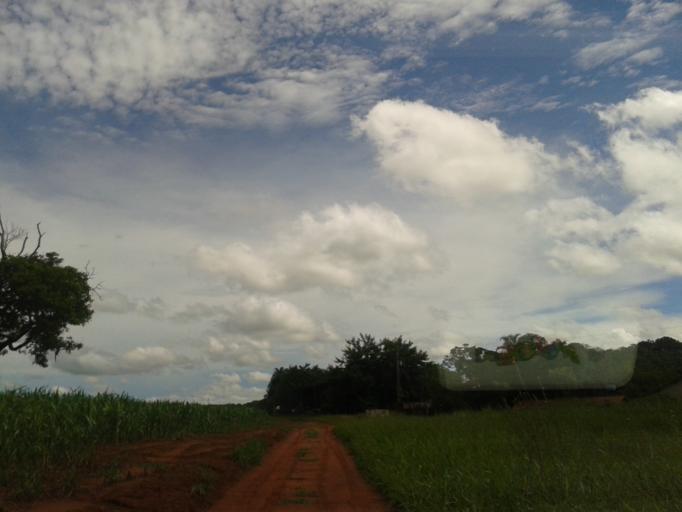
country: BR
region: Minas Gerais
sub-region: Santa Vitoria
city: Santa Vitoria
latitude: -19.1411
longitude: -50.4866
